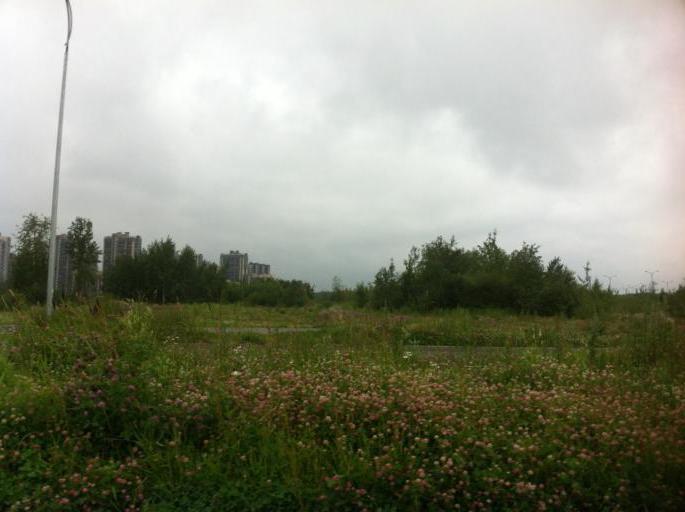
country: RU
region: St.-Petersburg
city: Sosnovaya Polyana
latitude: 59.8576
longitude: 30.1555
